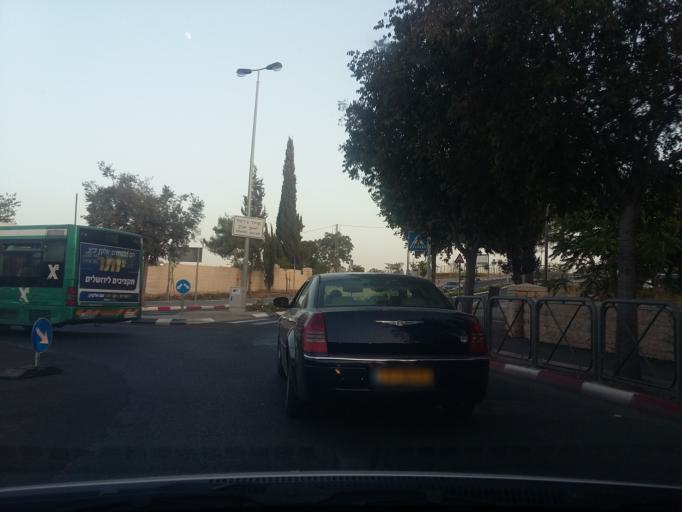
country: PS
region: West Bank
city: East Jerusalem
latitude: 31.7952
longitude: 35.2343
